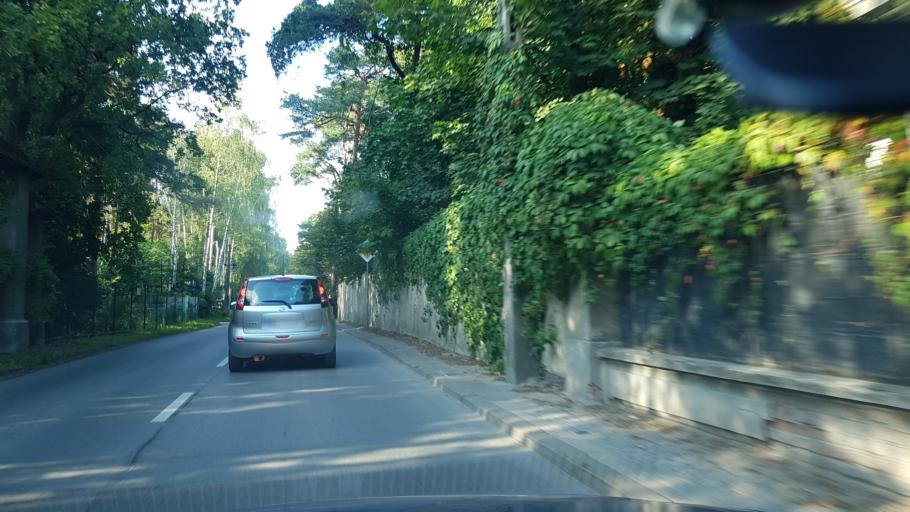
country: PL
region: Masovian Voivodeship
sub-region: Powiat piaseczynski
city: Konstancin-Jeziorna
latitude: 52.0722
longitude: 21.0992
